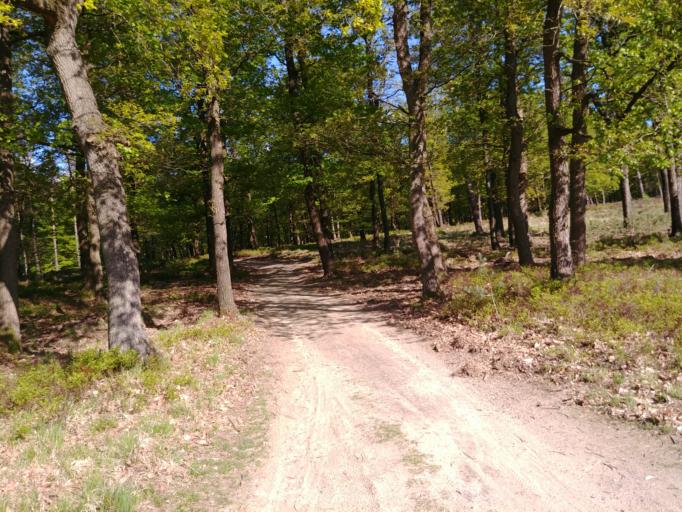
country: NL
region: Gelderland
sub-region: Gemeente Apeldoorn
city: Uddel
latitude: 52.2574
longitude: 5.8624
